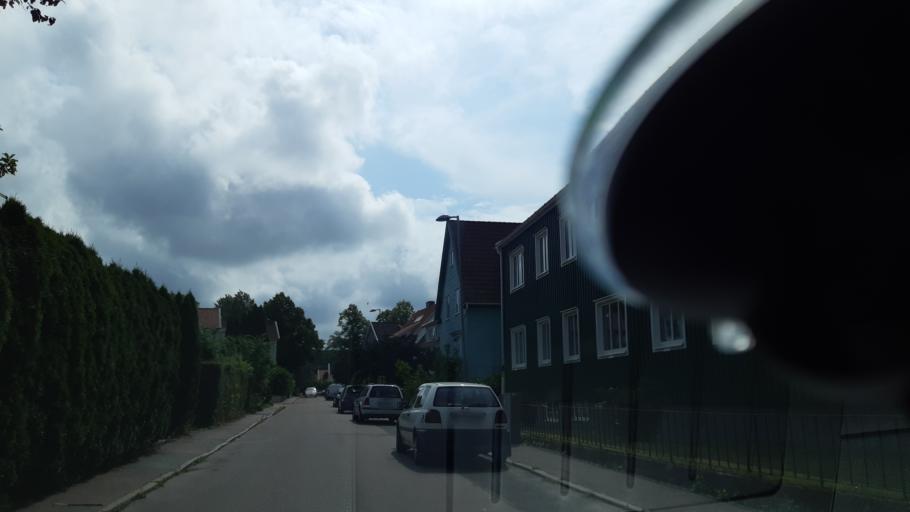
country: SE
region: Vaestra Goetaland
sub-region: Goteborg
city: Eriksbo
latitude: 57.7147
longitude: 12.0290
